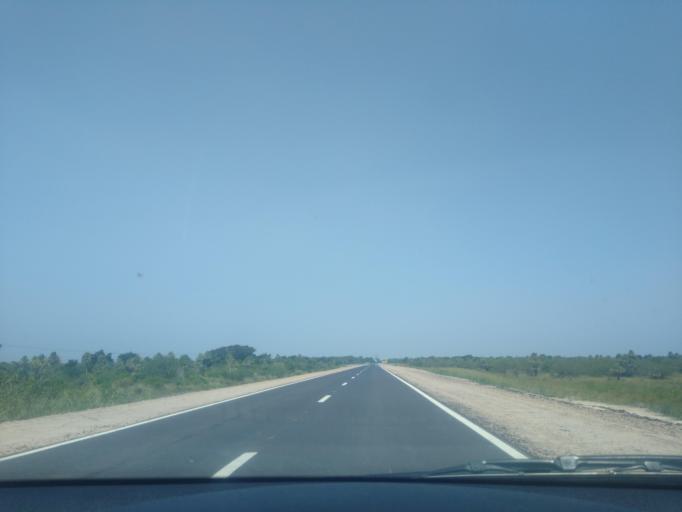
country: AR
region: Chaco
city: Puerto Tirol
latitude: -27.5710
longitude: -59.2659
